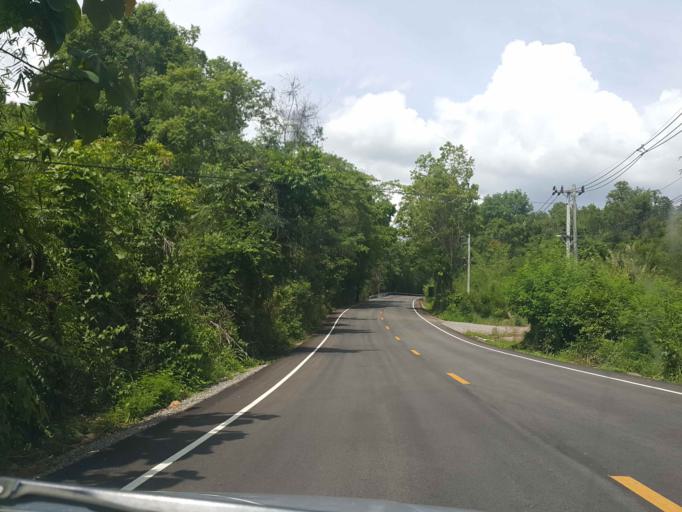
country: TH
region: Nan
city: Ban Luang
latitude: 18.8733
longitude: 100.5139
